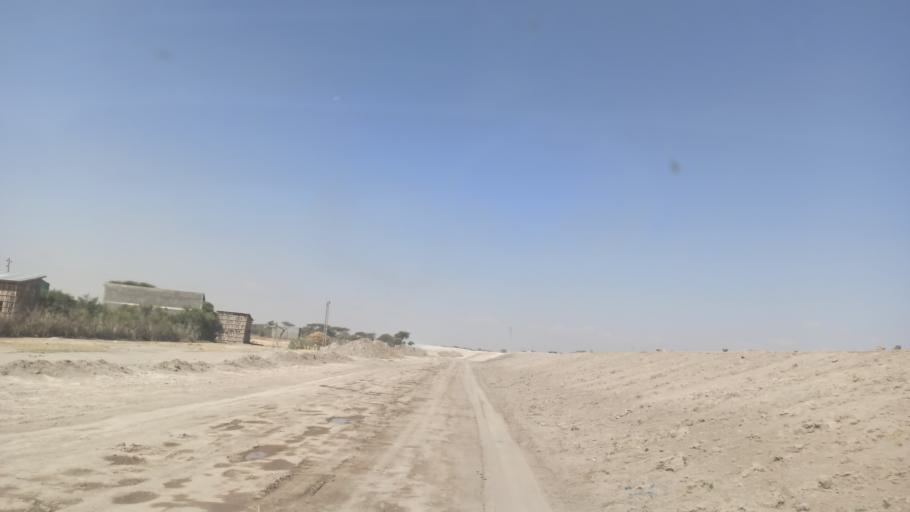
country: ET
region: Oromiya
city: Ziway
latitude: 7.6892
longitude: 38.6635
